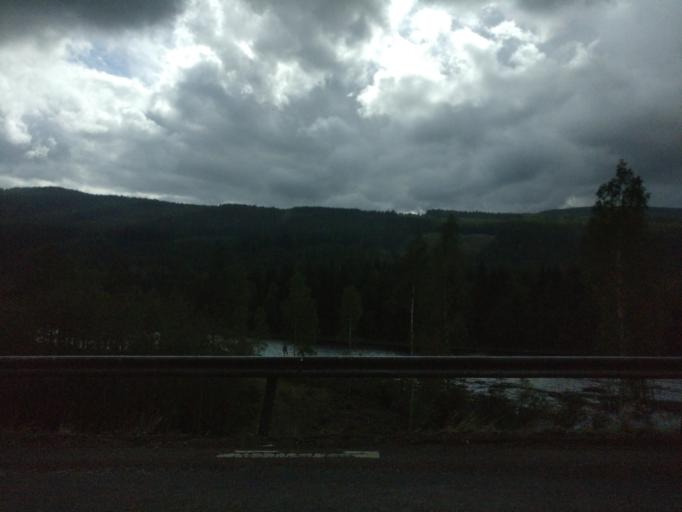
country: SE
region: Vaermland
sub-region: Torsby Kommun
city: Torsby
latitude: 60.7417
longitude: 12.8352
